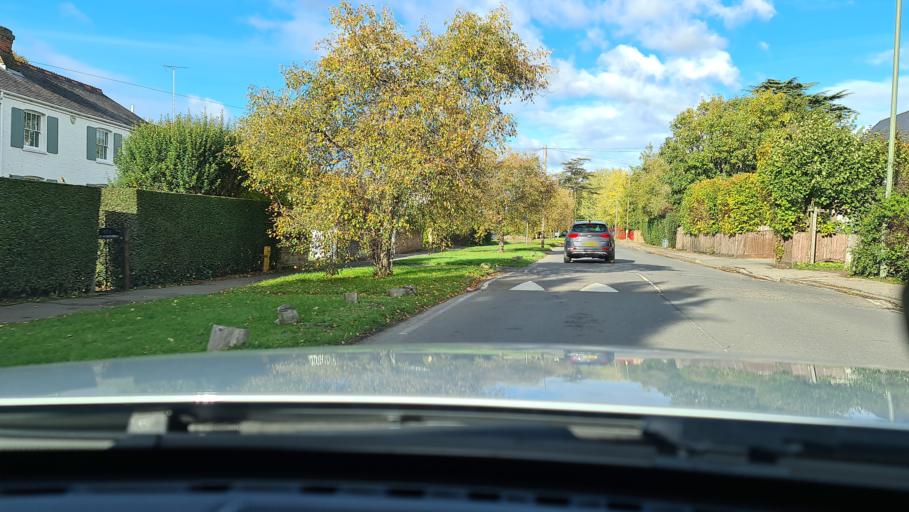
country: GB
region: England
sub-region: Surrey
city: Esher
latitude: 51.3639
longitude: -0.3789
